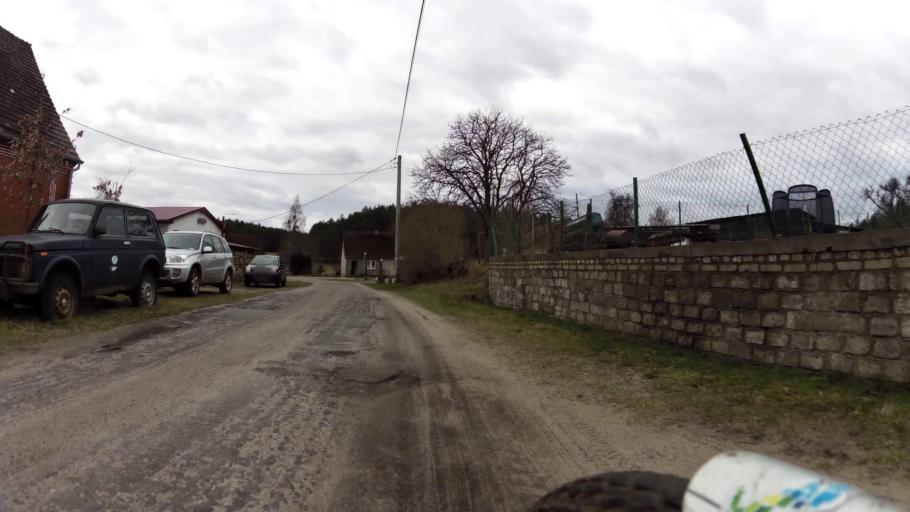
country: PL
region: Pomeranian Voivodeship
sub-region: Powiat bytowski
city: Trzebielino
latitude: 54.1390
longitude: 17.1485
